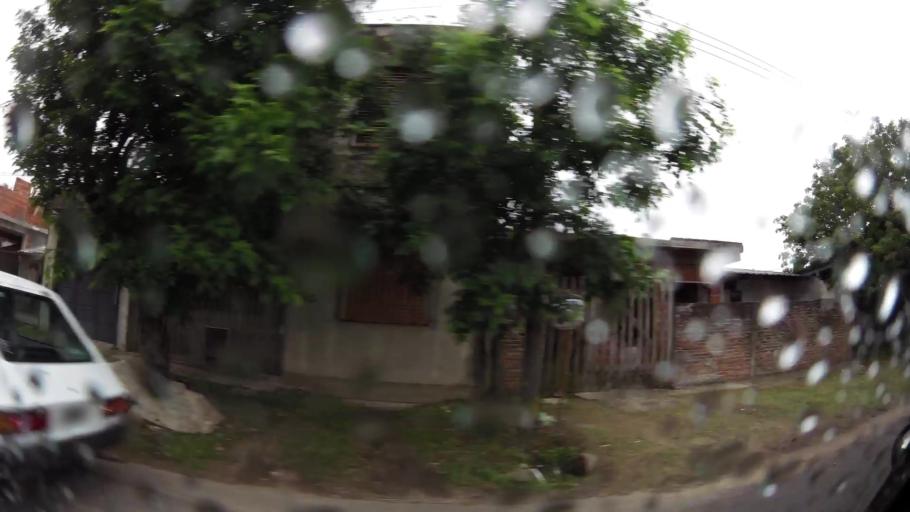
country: AR
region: Buenos Aires
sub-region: Partido de Quilmes
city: Quilmes
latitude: -34.7792
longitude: -58.2328
